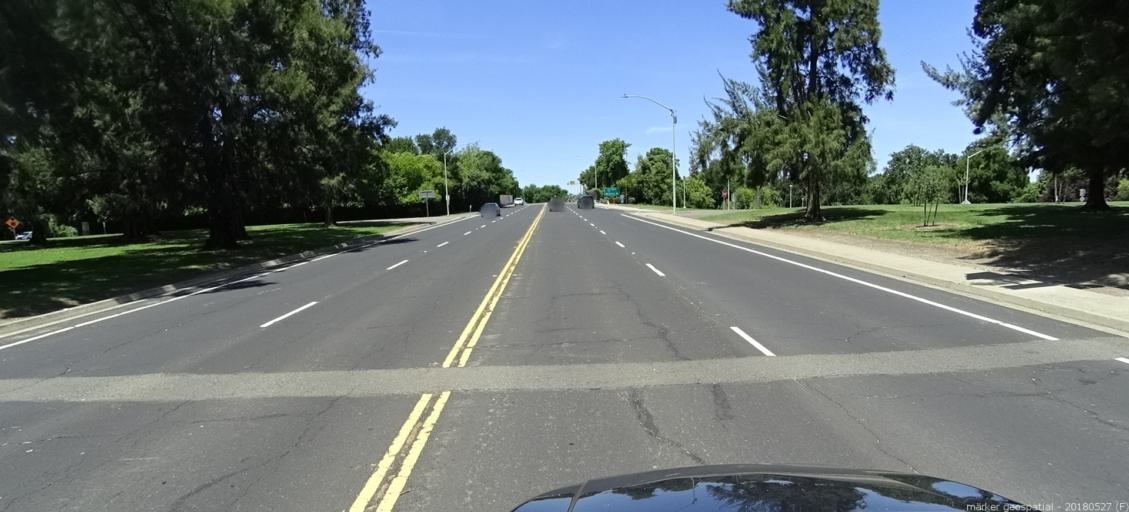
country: US
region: California
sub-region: Sacramento County
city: Sacramento
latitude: 38.5398
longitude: -121.5085
